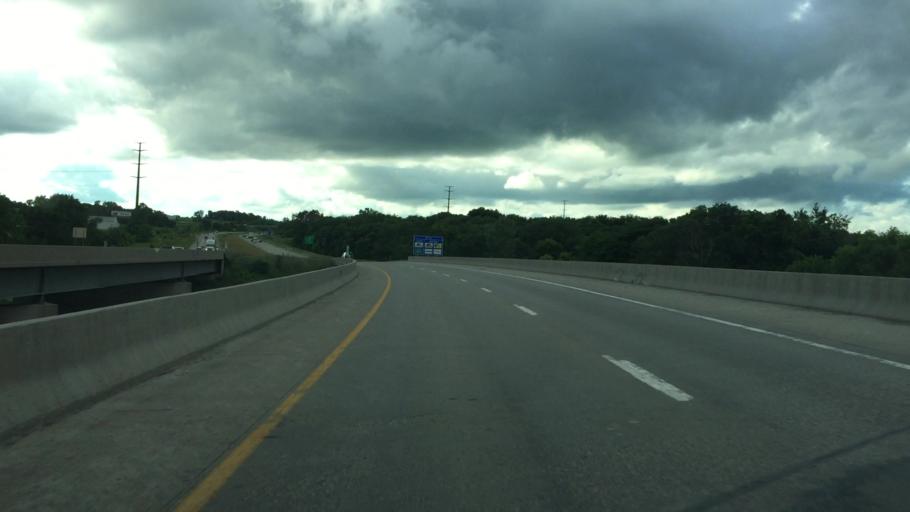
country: US
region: Iowa
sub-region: Polk County
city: Altoona
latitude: 41.6231
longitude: -93.4939
